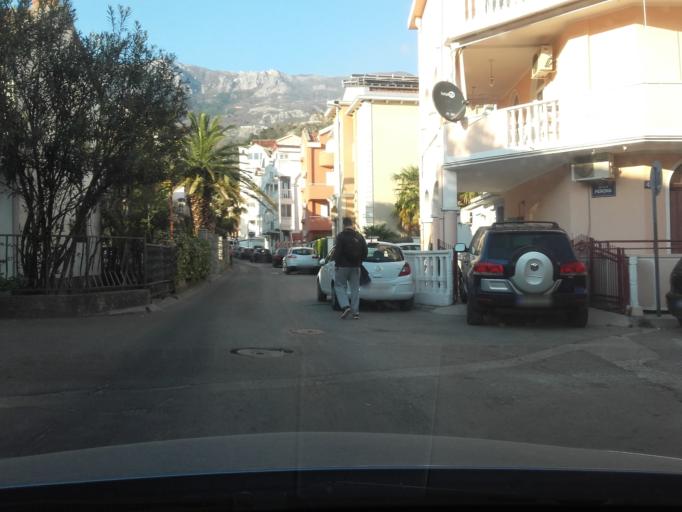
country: ME
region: Budva
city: Budva
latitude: 42.2918
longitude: 18.8474
